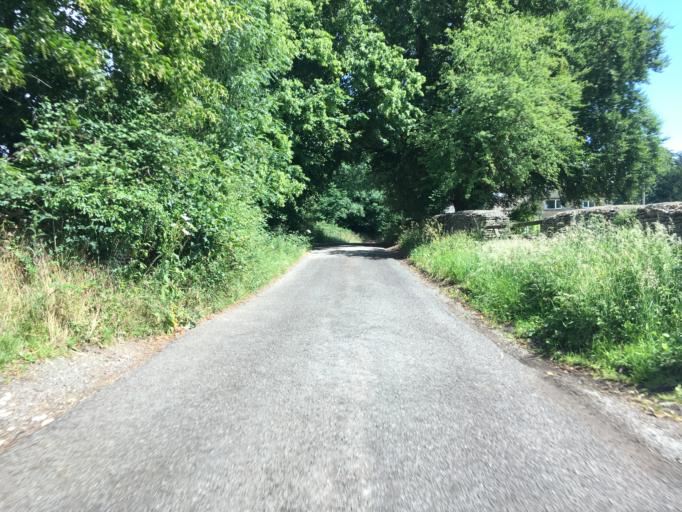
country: GB
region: England
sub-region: Gloucestershire
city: Tetbury
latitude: 51.6565
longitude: -2.1870
